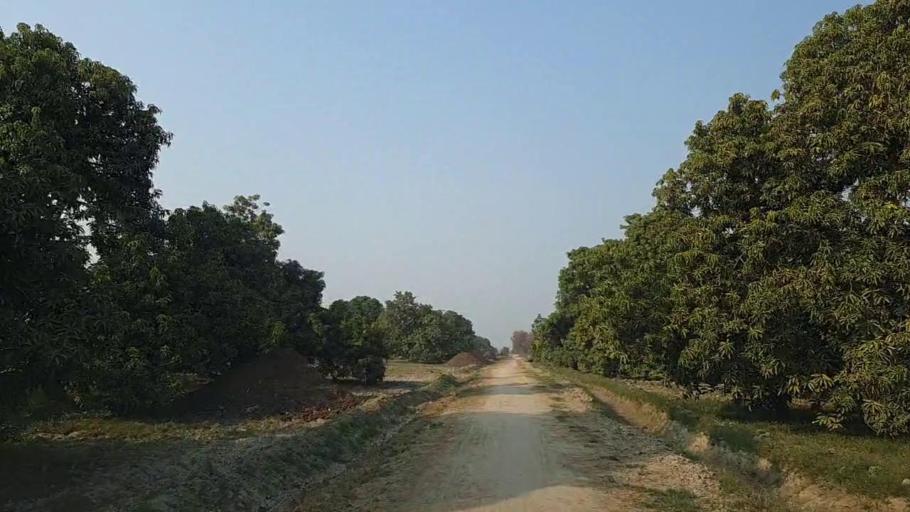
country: PK
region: Sindh
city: Sann
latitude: 26.1083
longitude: 68.1617
